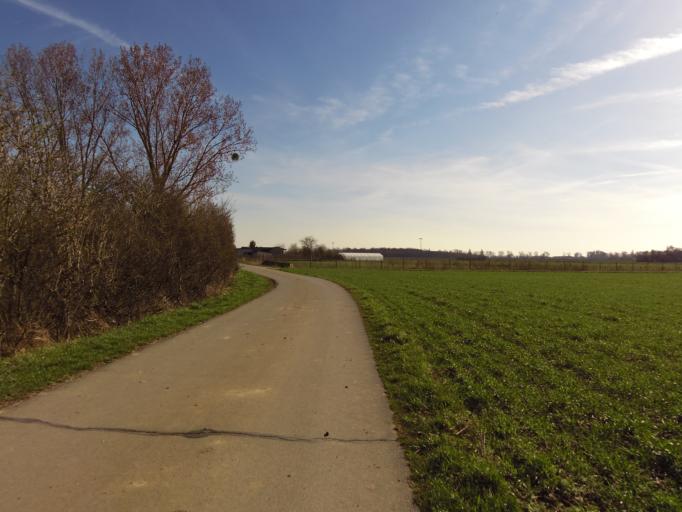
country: DE
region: Hesse
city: Biebesheim
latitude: 49.7845
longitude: 8.4366
